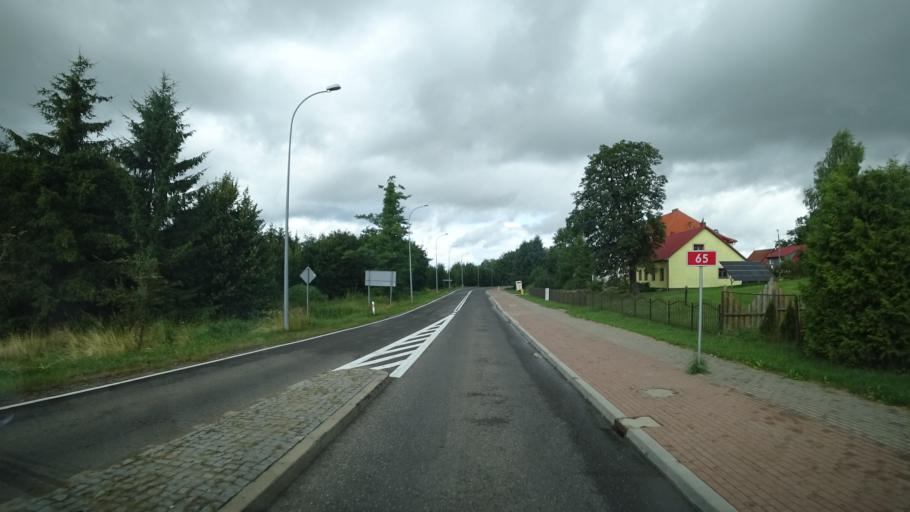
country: PL
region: Warmian-Masurian Voivodeship
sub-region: Powiat olecki
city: Kowale Oleckie
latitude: 54.1691
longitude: 22.4143
